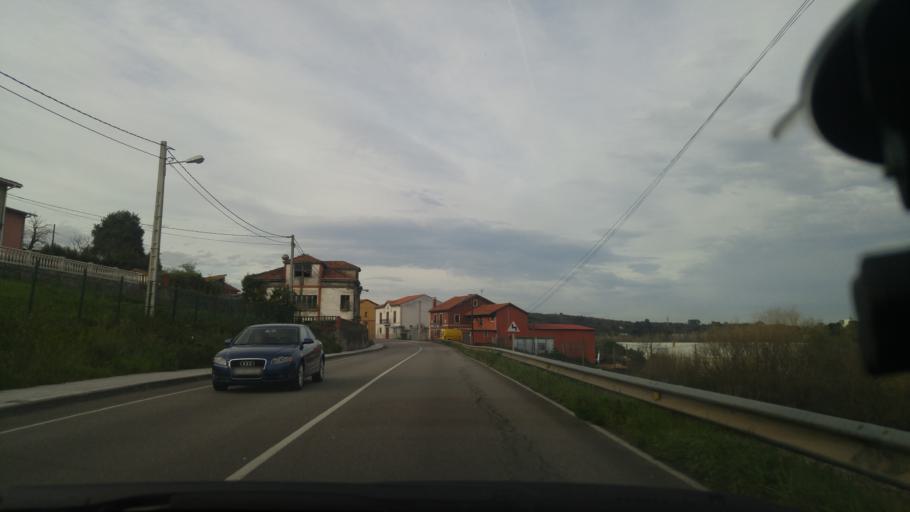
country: ES
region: Asturias
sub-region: Province of Asturias
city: Corvera de Asturias
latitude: 43.5208
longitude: -5.8707
